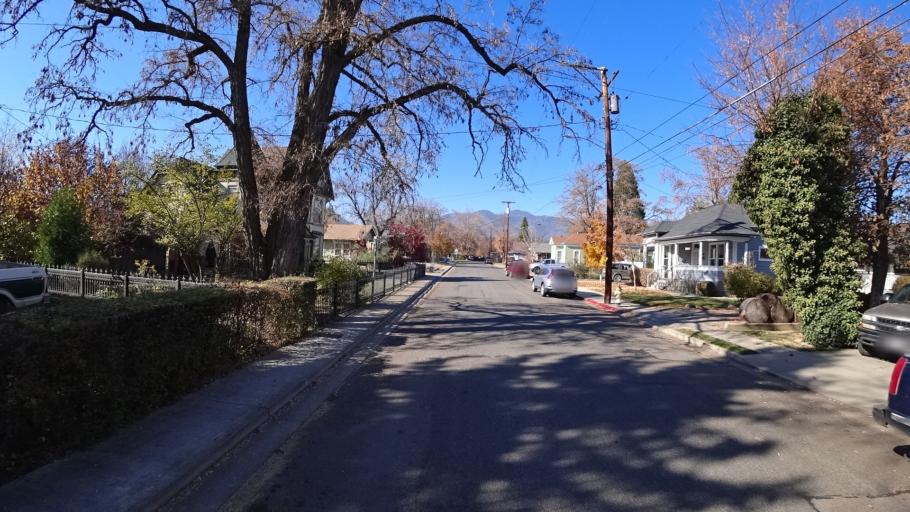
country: US
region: California
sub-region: Siskiyou County
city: Yreka
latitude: 41.7301
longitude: -122.6406
